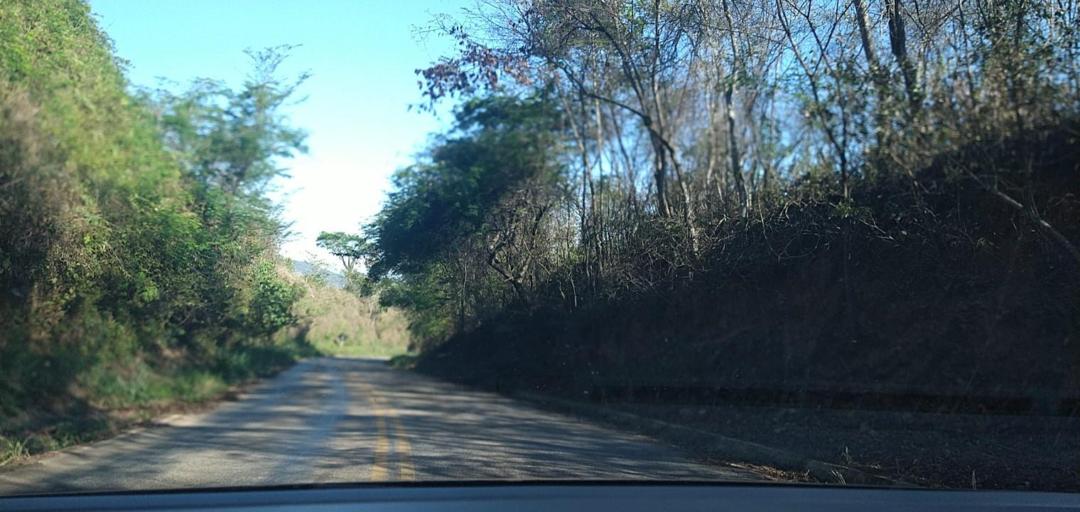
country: BR
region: Minas Gerais
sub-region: Ponte Nova
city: Ponte Nova
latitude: -20.2350
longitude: -42.9011
